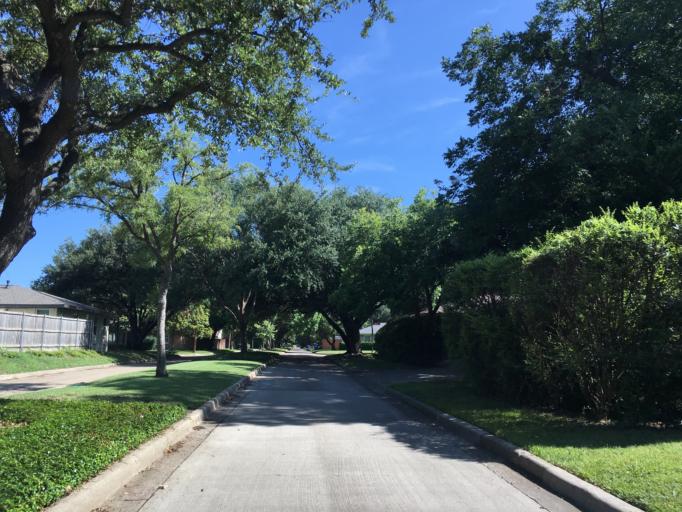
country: US
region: Texas
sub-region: Dallas County
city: Farmers Branch
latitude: 32.9195
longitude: -96.8768
